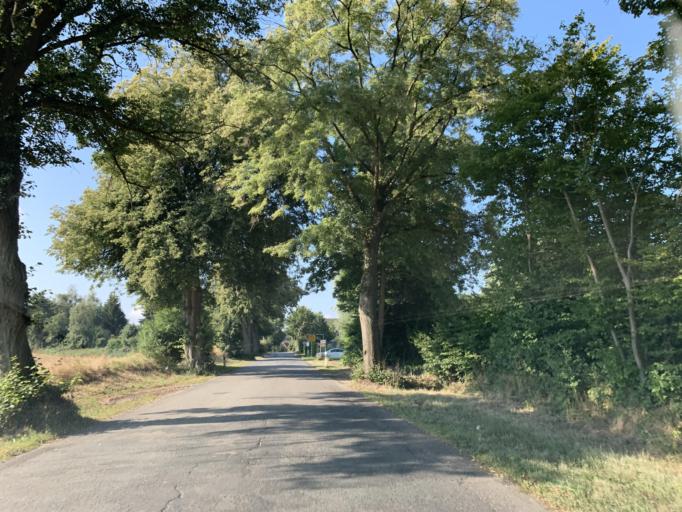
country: DE
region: Mecklenburg-Vorpommern
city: Blankensee
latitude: 53.3347
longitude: 13.3442
